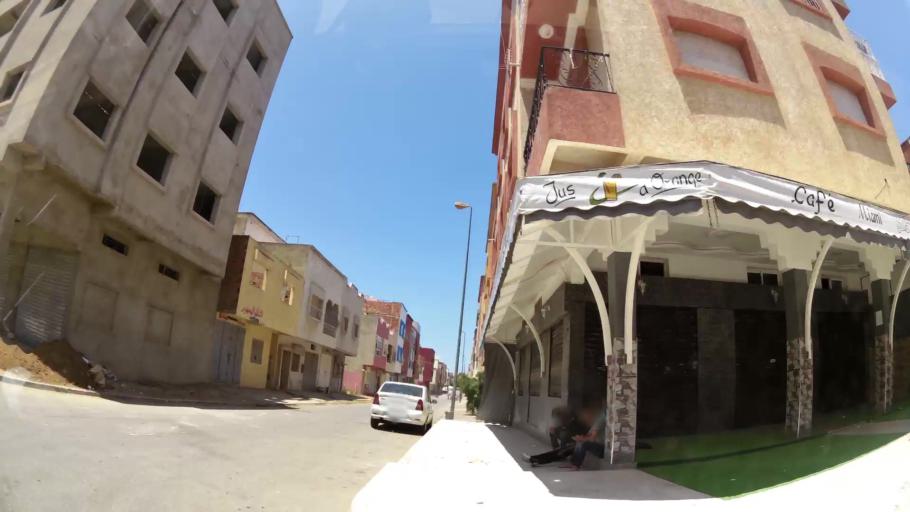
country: MA
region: Gharb-Chrarda-Beni Hssen
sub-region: Kenitra Province
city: Kenitra
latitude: 34.2522
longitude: -6.6251
